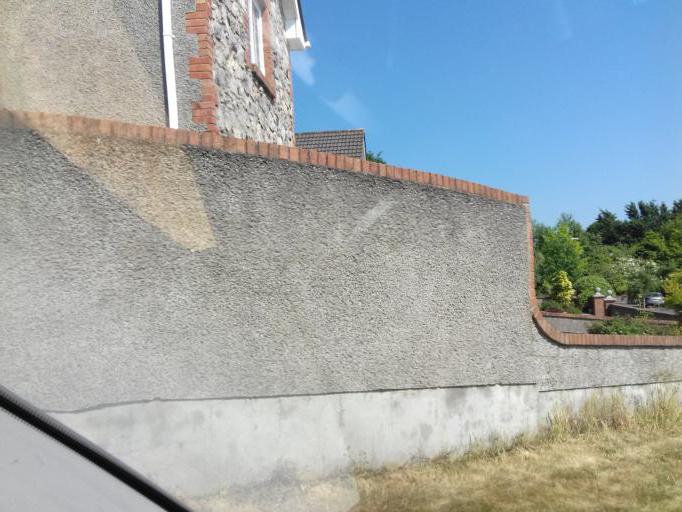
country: IE
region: Leinster
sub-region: An Mhi
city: Slane
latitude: 53.7109
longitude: -6.5445
